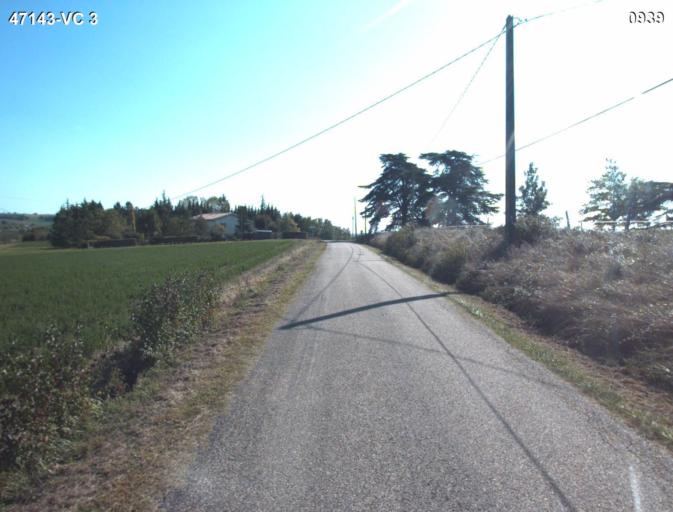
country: FR
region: Aquitaine
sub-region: Departement du Lot-et-Garonne
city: Lavardac
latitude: 44.1918
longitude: 0.2944
